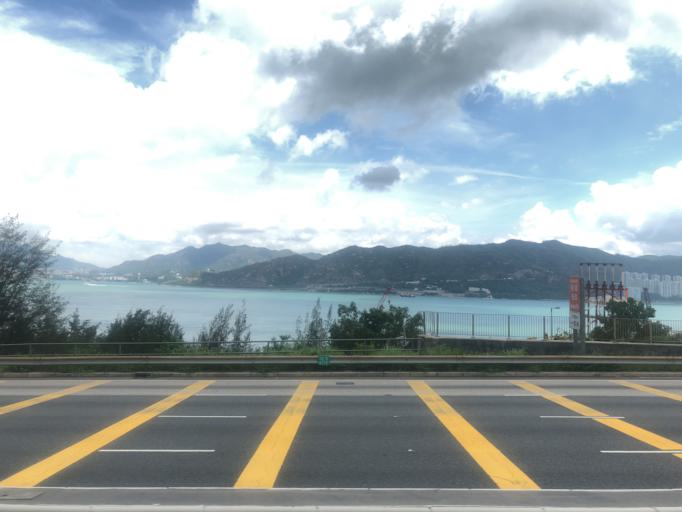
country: HK
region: Tsuen Wan
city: Tsuen Wan
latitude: 22.3377
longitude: 114.0404
